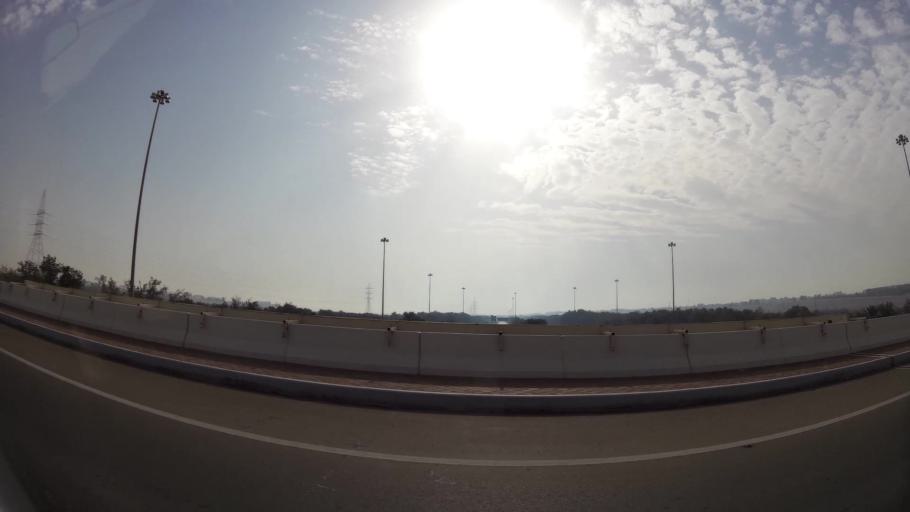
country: AE
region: Abu Dhabi
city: Abu Dhabi
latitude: 24.2525
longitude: 54.7086
